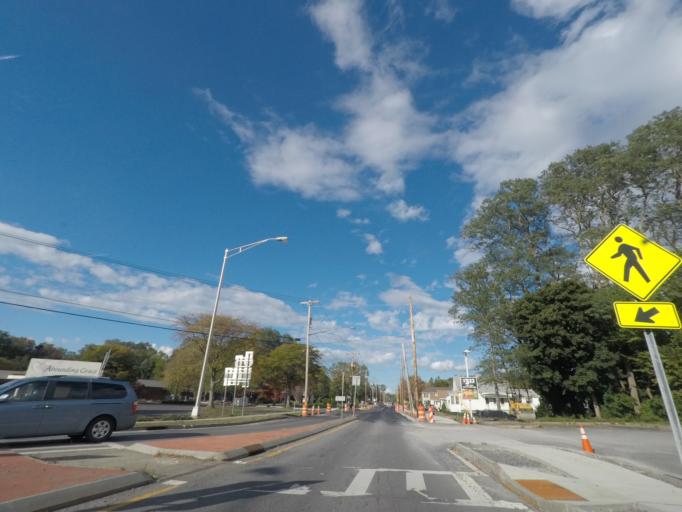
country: US
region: New York
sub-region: Schenectady County
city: Rotterdam
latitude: 42.7652
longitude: -73.9385
